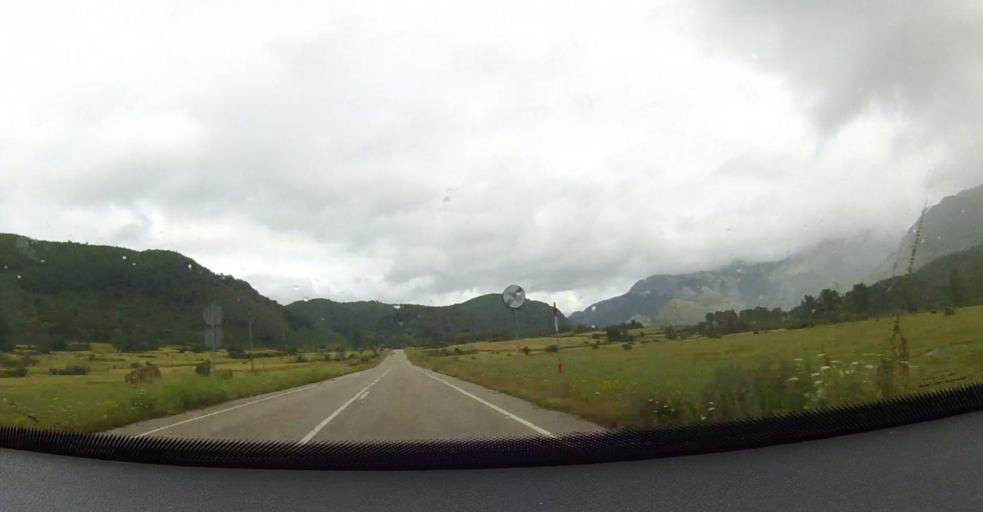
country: ES
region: Castille and Leon
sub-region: Provincia de Leon
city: Acebedo
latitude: 43.0396
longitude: -5.0890
